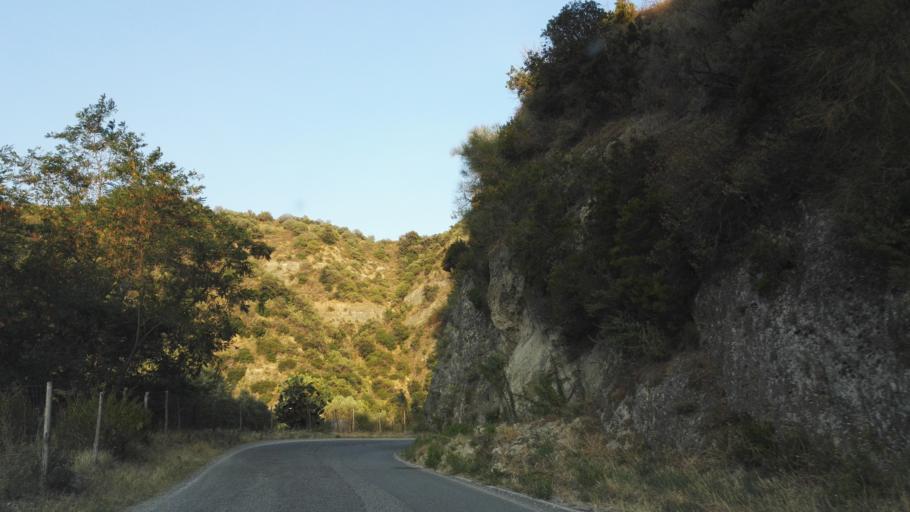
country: IT
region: Calabria
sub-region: Provincia di Reggio Calabria
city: Caulonia
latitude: 38.4003
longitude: 16.4128
